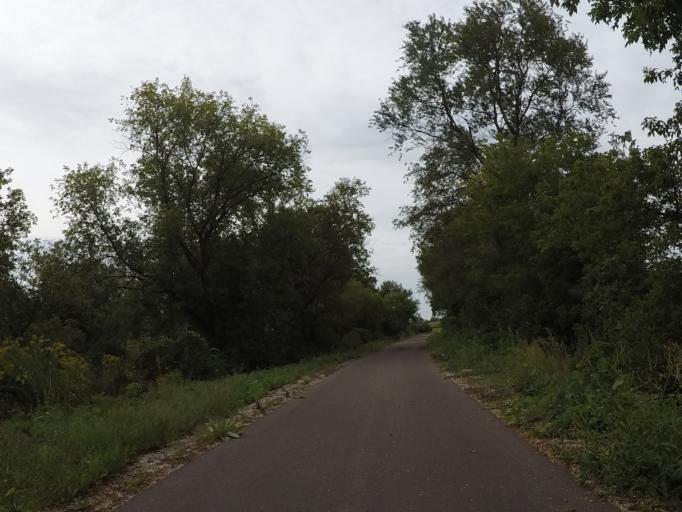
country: US
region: Wisconsin
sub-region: Sauk County
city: Prairie du Sac
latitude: 43.3456
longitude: -89.7410
